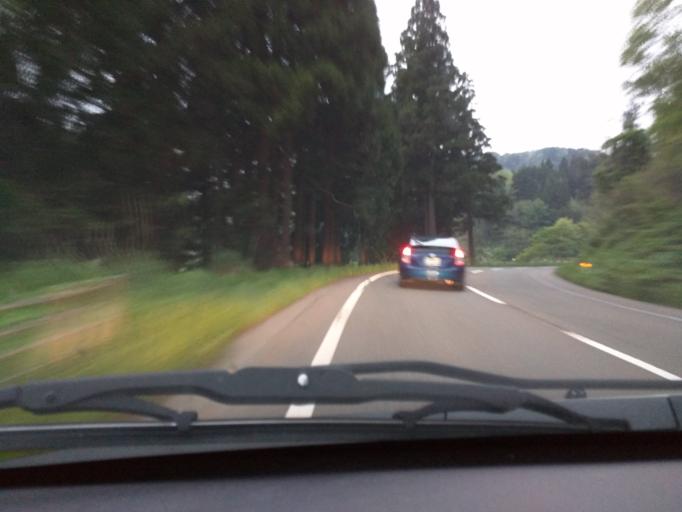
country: JP
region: Niigata
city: Ojiya
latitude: 37.3218
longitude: 138.6853
